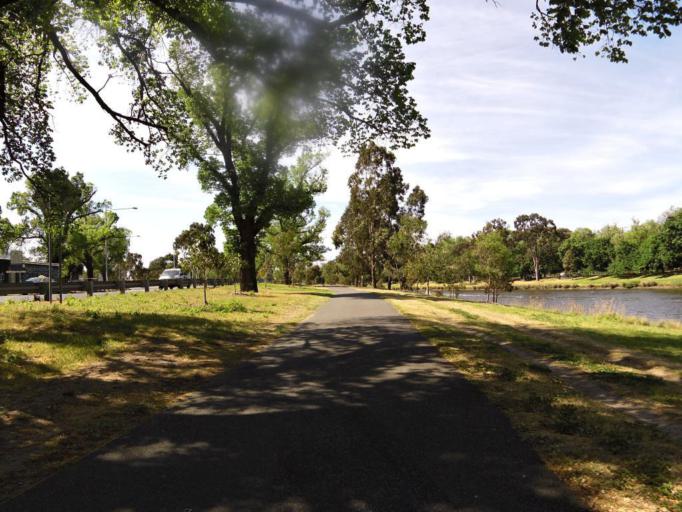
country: AU
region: Victoria
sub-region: Melbourne
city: East Melbourne
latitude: -37.8256
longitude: 144.9803
